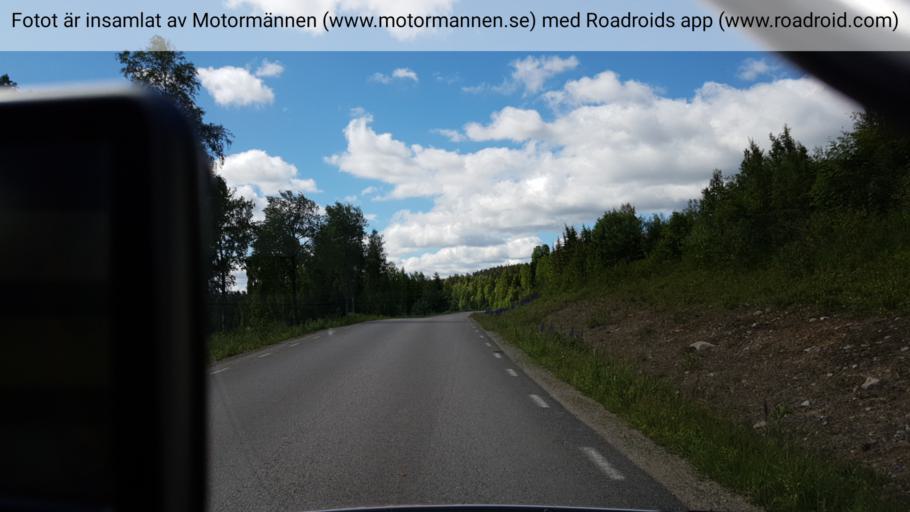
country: SE
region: Gaevleborg
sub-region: Hudiksvalls Kommun
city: Sorforsa
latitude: 61.6634
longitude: 16.9267
